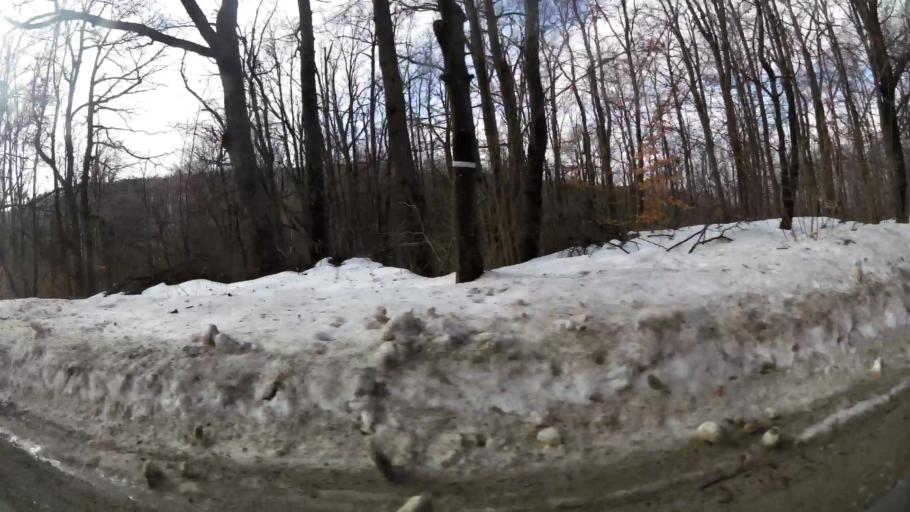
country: BG
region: Sofiya
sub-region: Obshtina Bozhurishte
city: Bozhurishte
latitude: 42.6341
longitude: 23.2226
